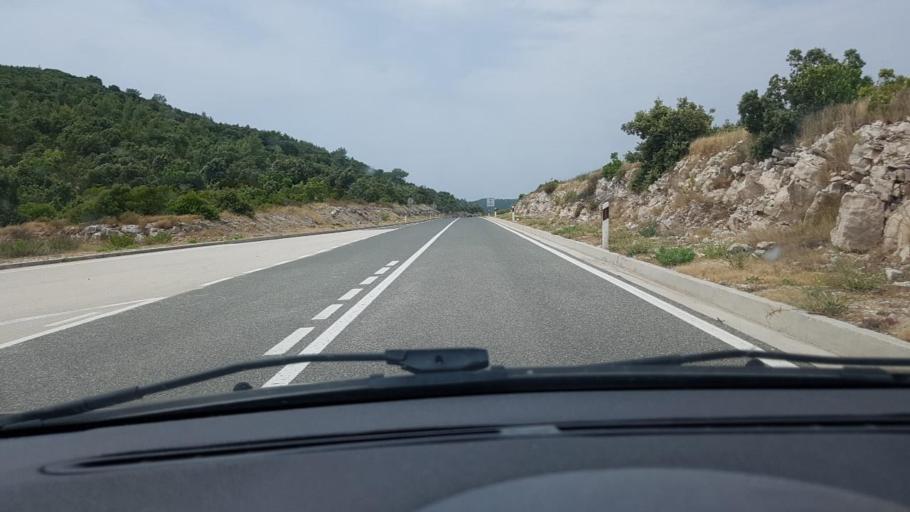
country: HR
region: Dubrovacko-Neretvanska
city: Smokvica
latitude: 42.9548
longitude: 16.9166
